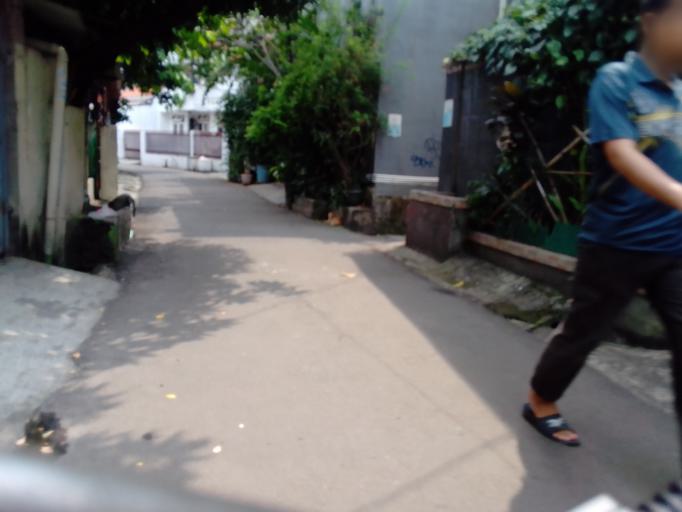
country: ID
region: Jakarta Raya
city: Jakarta
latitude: -6.2156
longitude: 106.8134
